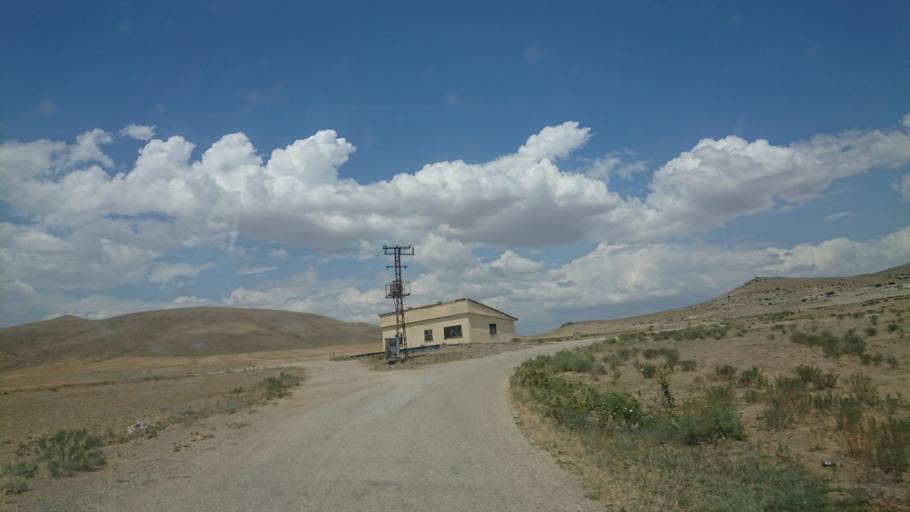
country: TR
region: Aksaray
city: Sariyahsi
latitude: 39.0049
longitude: 33.9103
